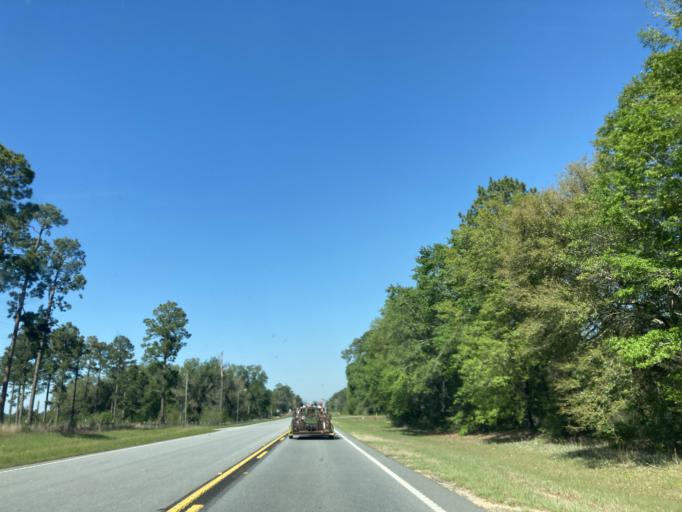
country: US
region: Georgia
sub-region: Baker County
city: Newton
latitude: 31.4456
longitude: -84.2659
